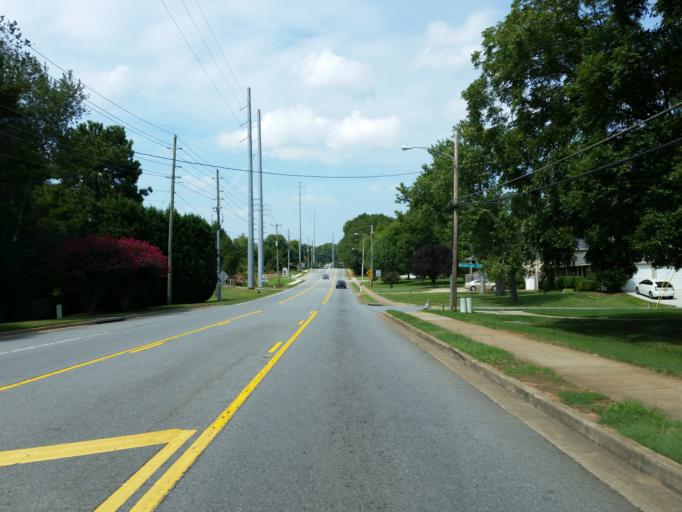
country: US
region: Georgia
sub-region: Cobb County
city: Marietta
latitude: 33.9905
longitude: -84.5078
